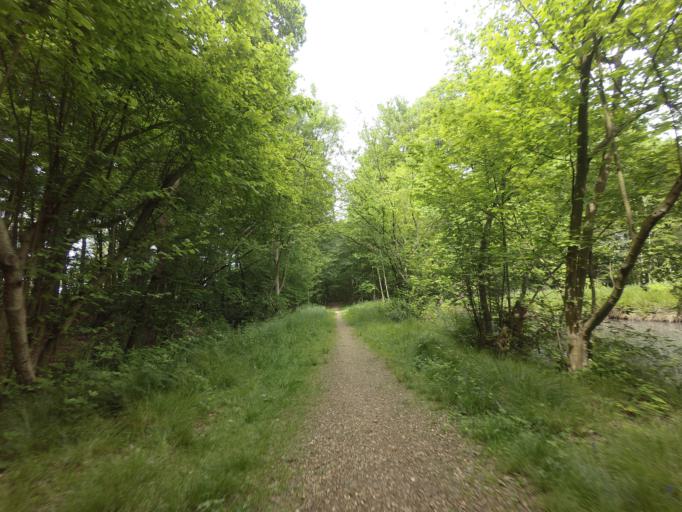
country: BE
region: Flanders
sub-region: Provincie Antwerpen
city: Bornem
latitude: 51.1079
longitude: 4.2757
